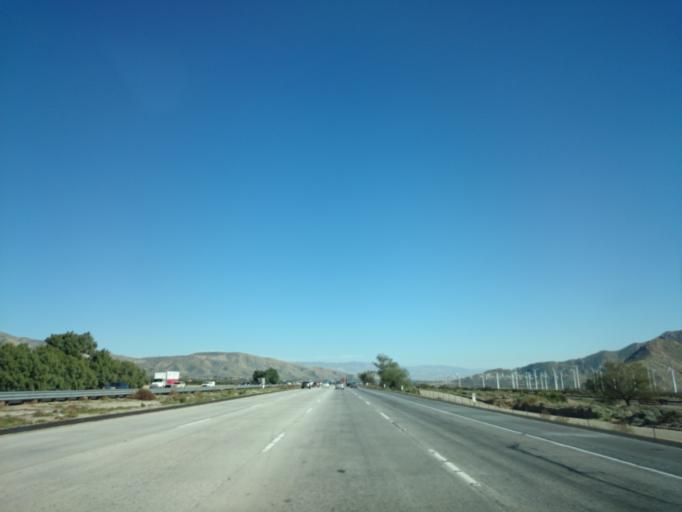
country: US
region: California
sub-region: Riverside County
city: Cabazon
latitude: 33.9210
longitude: -116.7520
